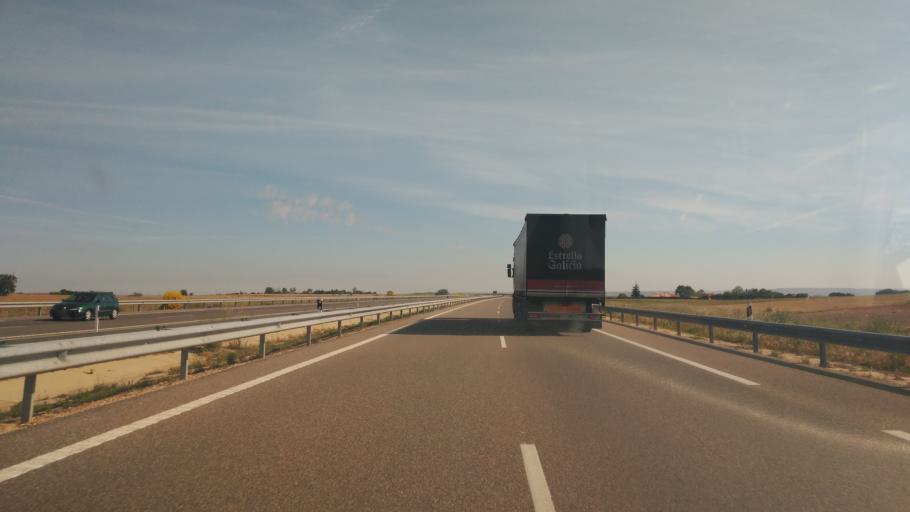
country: ES
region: Castille and Leon
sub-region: Provincia de Zamora
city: Morales del Vino
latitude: 41.4331
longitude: -5.7212
